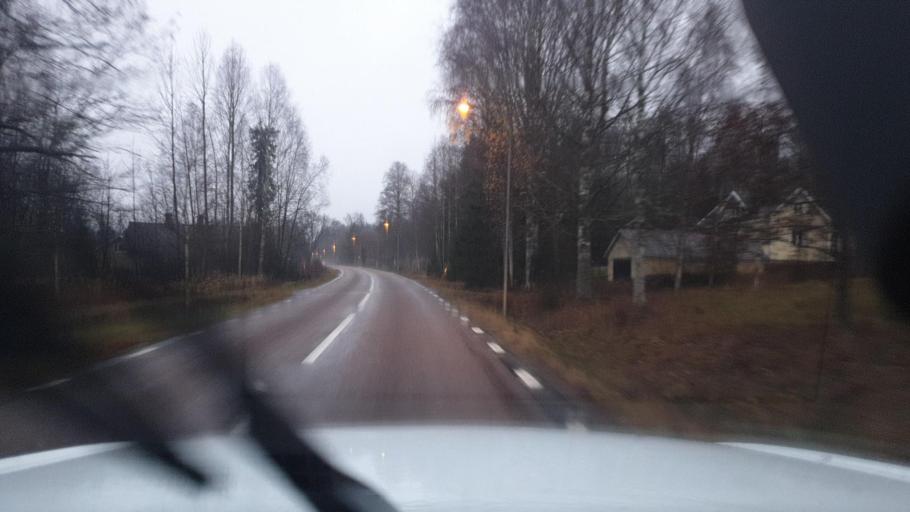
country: SE
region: Vaermland
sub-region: Sunne Kommun
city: Sunne
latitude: 59.8904
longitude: 12.9202
